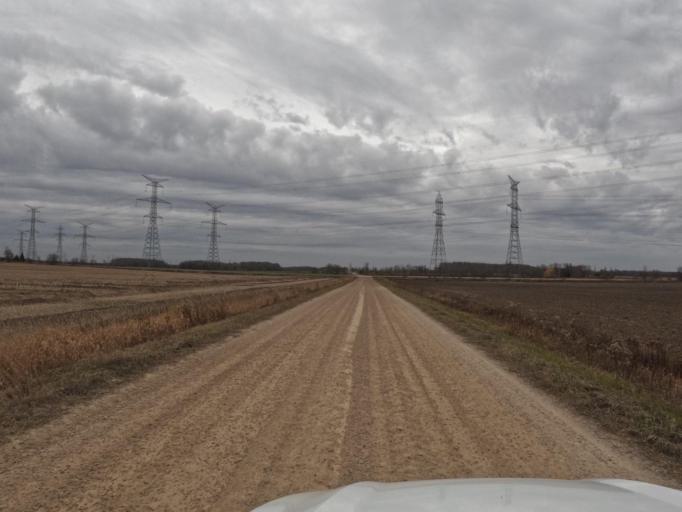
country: CA
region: Ontario
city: Shelburne
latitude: 43.9891
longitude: -80.3844
